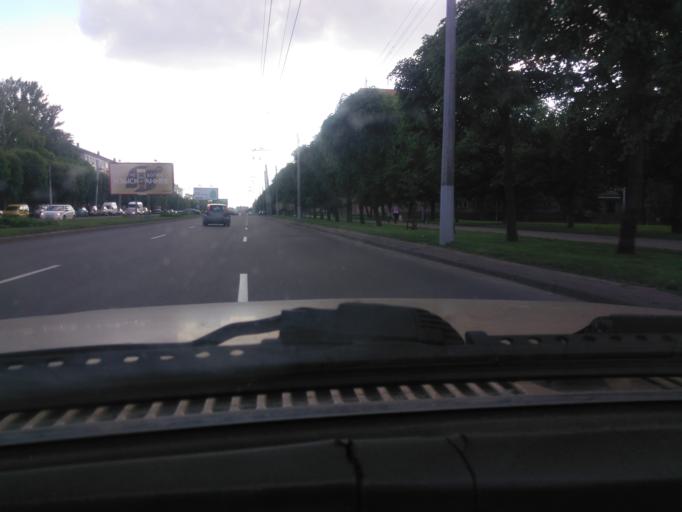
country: BY
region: Mogilev
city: Mahilyow
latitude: 53.9113
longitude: 30.3157
